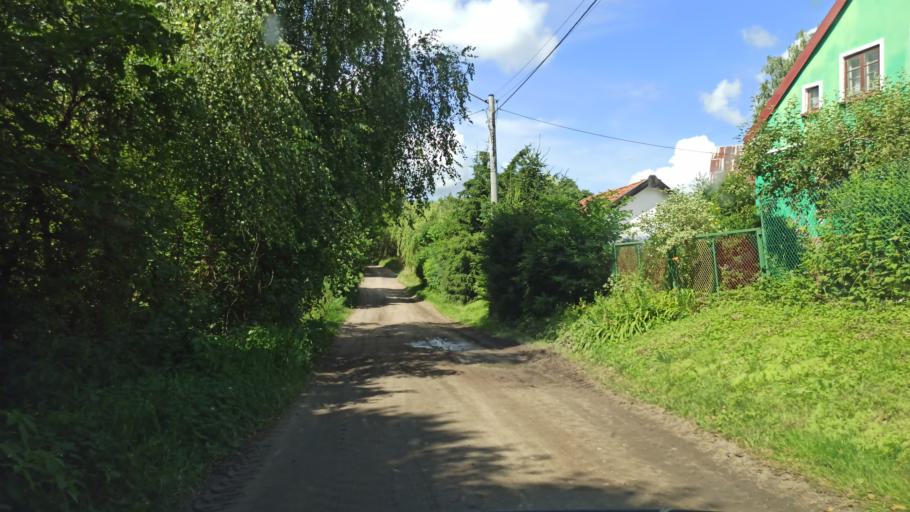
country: PL
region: Warmian-Masurian Voivodeship
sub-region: Powiat ostrodzki
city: Morag
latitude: 53.8615
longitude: 20.0624
